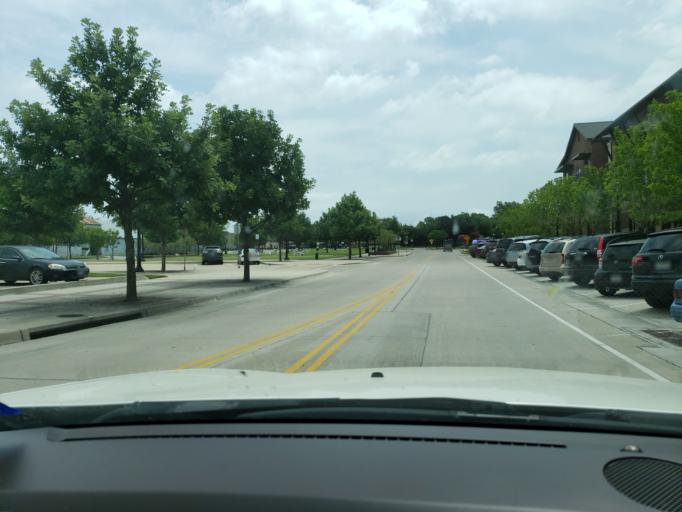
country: US
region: Texas
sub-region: Dallas County
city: Rowlett
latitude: 32.9030
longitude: -96.5649
